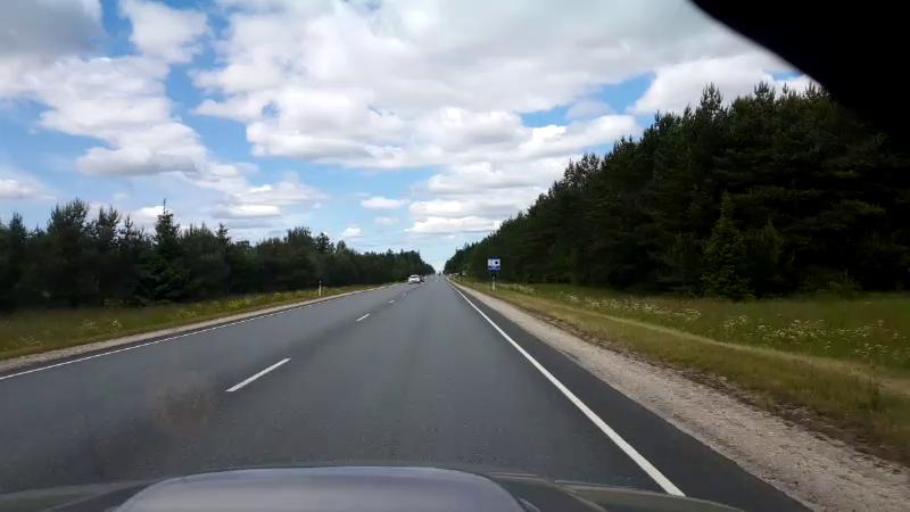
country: EE
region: Raplamaa
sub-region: Maerjamaa vald
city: Marjamaa
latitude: 58.9896
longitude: 24.4676
